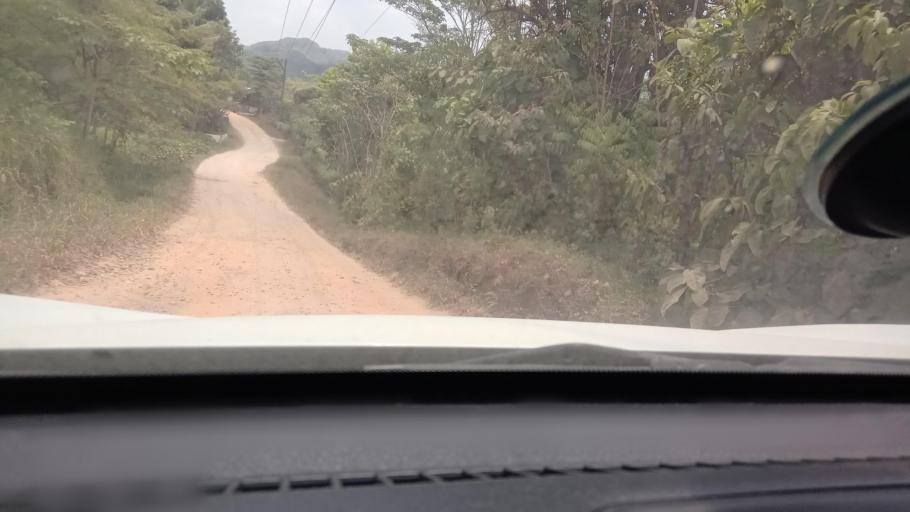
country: MX
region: Tabasco
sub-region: Huimanguillo
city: Francisco Rueda
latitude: 17.5226
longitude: -93.8846
